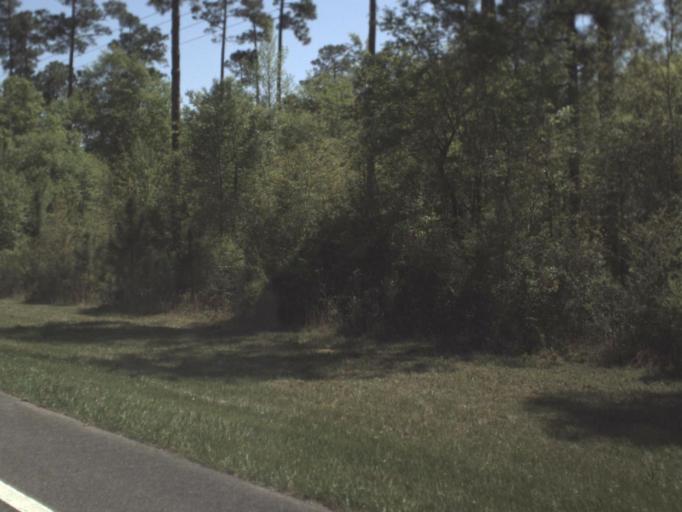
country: US
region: Florida
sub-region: Santa Rosa County
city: Point Baker
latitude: 30.8769
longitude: -86.9460
